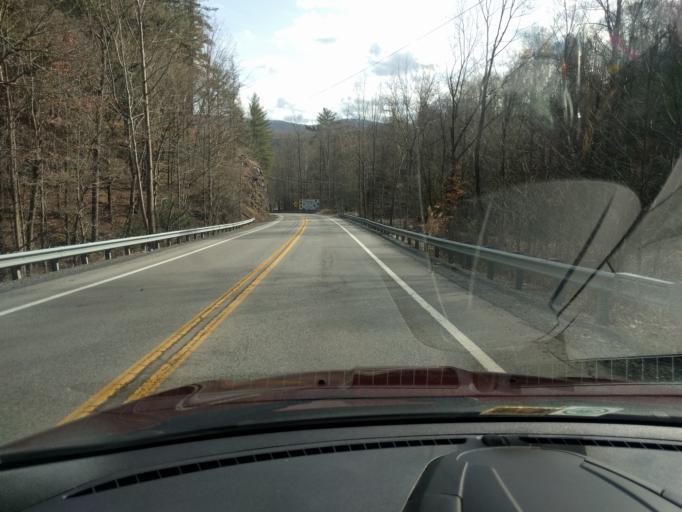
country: US
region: West Virginia
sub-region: Greenbrier County
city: Lewisburg
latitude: 37.7875
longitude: -80.4046
